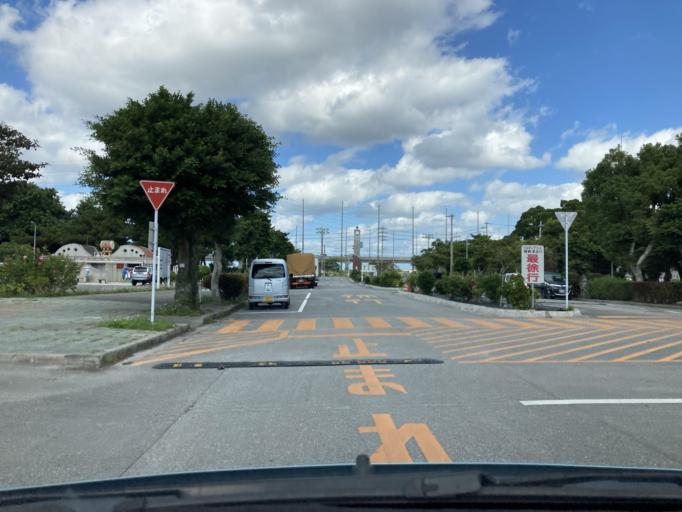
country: JP
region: Okinawa
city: Okinawa
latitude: 26.3332
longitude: 127.7874
